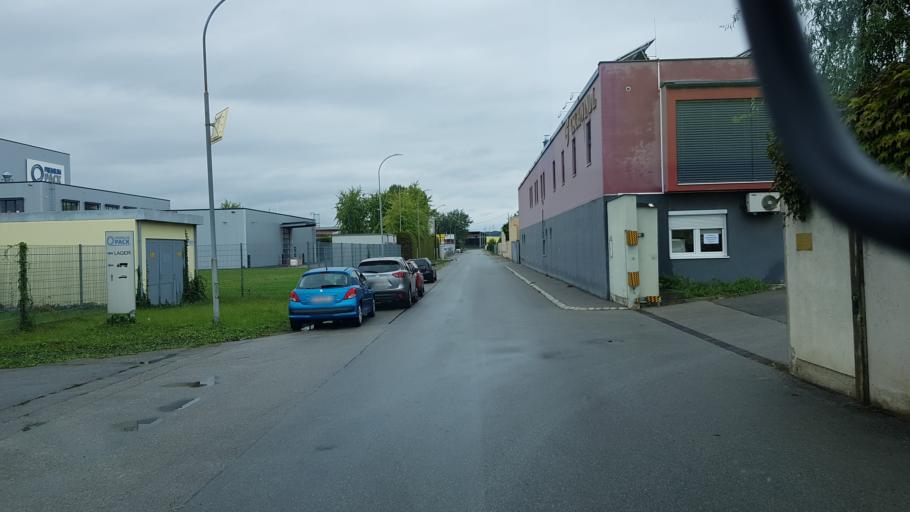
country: AT
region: Lower Austria
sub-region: Politischer Bezirk Mistelbach
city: Grossebersdorf
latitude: 48.3380
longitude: 16.4609
